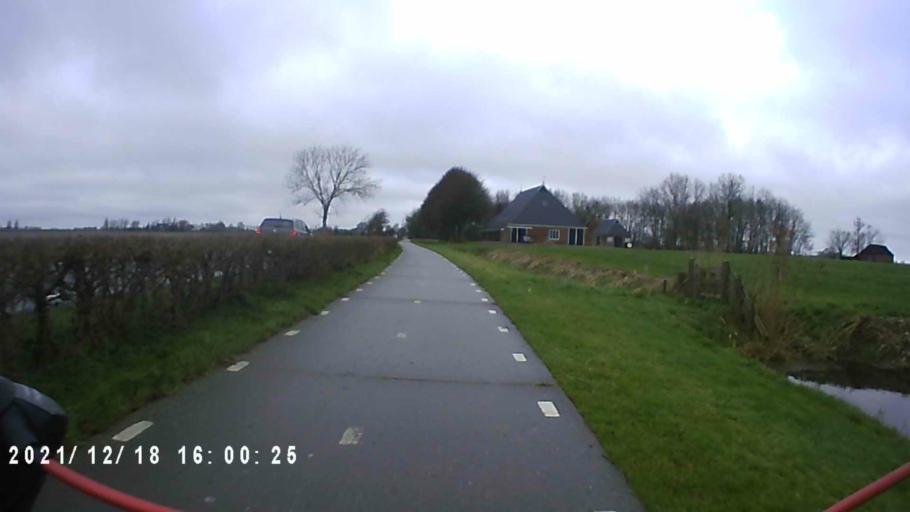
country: NL
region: Friesland
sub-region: Gemeente Dongeradeel
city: Anjum
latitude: 53.3421
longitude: 6.0883
